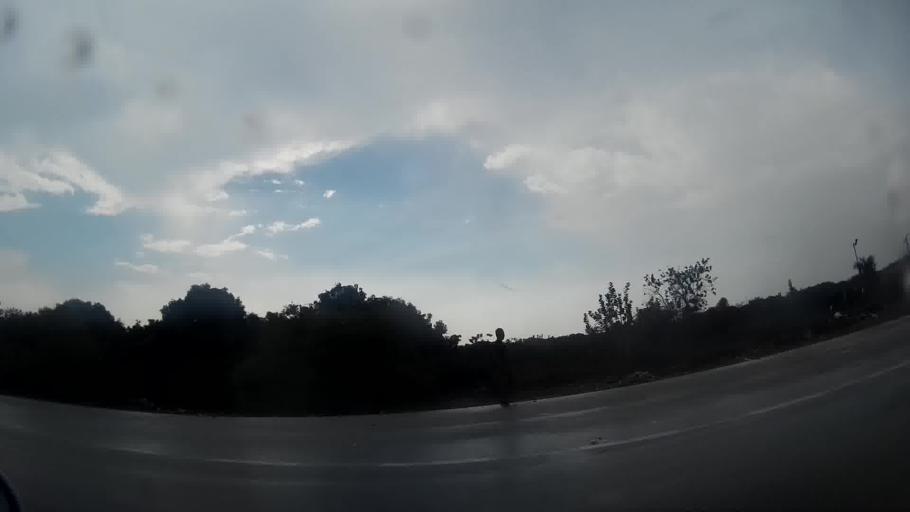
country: CO
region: Magdalena
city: Cienaga
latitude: 11.0229
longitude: -74.2086
